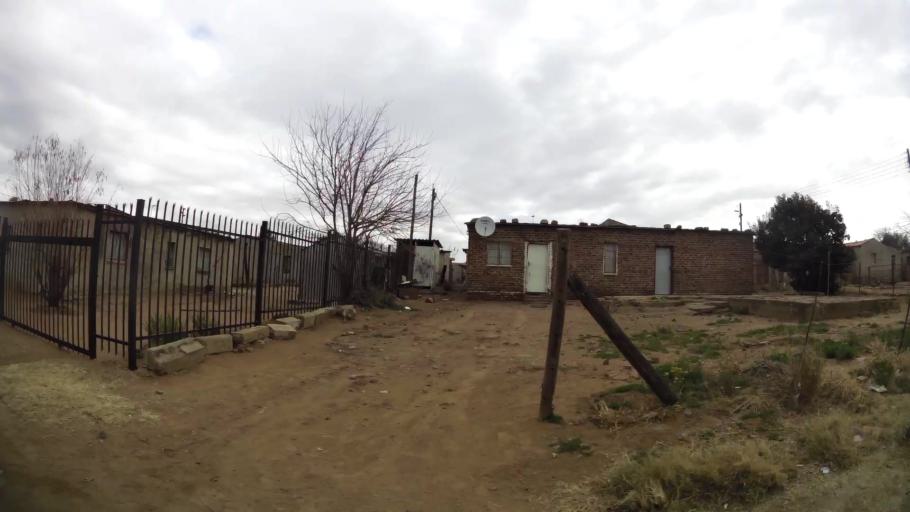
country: ZA
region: Orange Free State
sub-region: Fezile Dabi District Municipality
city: Kroonstad
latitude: -27.6474
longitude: 27.2069
